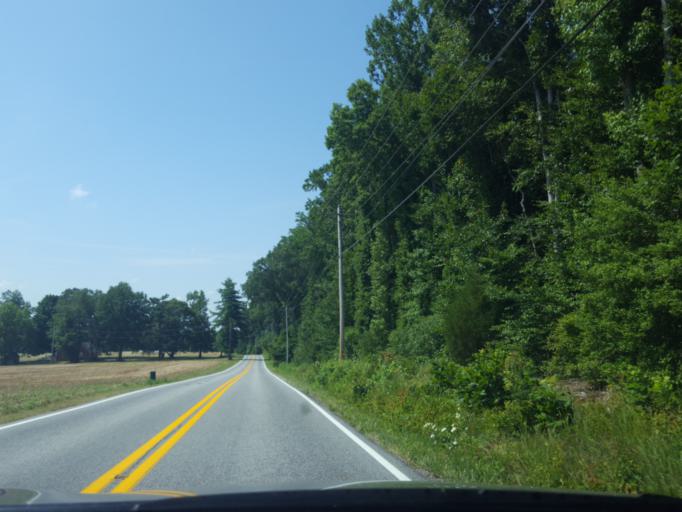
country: US
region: Maryland
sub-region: Saint Mary's County
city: Charlotte Hall
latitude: 38.4629
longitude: -76.8770
